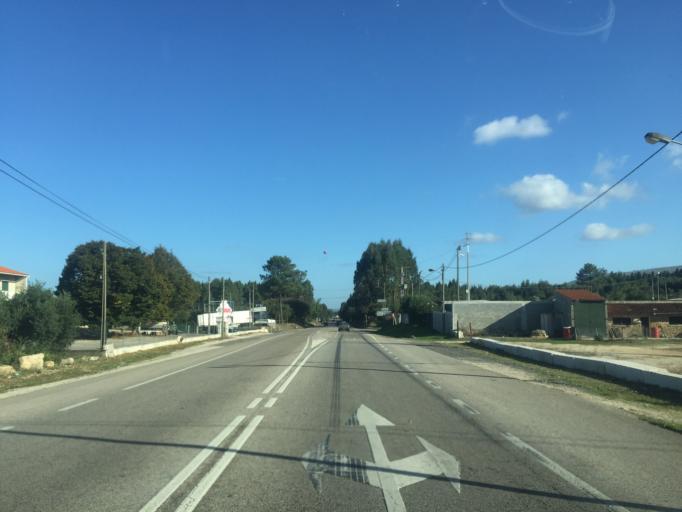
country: PT
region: Leiria
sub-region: Alcobaca
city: Turquel
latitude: 39.4917
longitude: -8.9321
